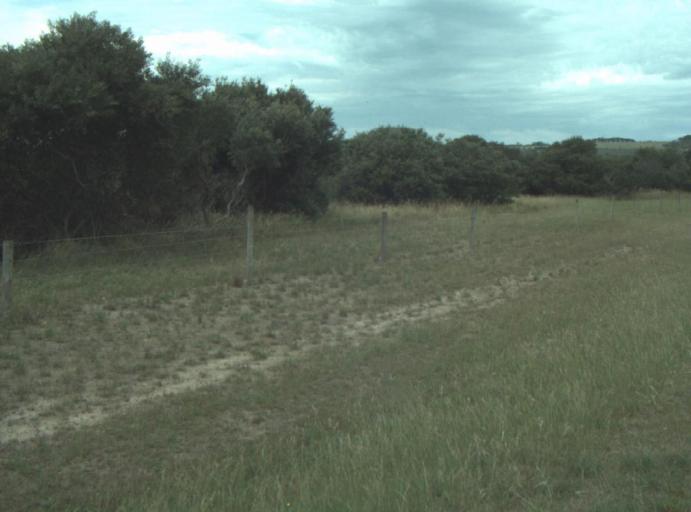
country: AU
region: Victoria
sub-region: Greater Geelong
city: Clifton Springs
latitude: -38.1113
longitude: 144.6295
